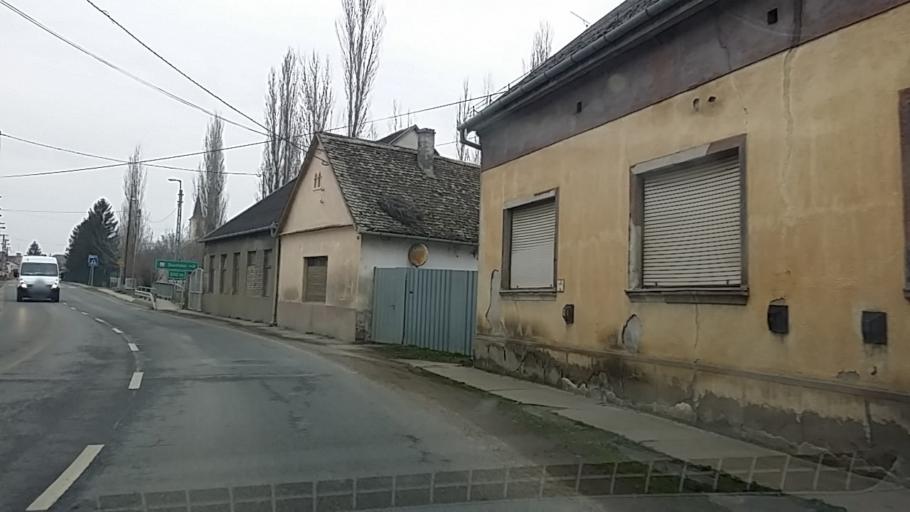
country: HU
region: Baranya
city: Dunaszekcso
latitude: 46.0833
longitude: 18.7590
